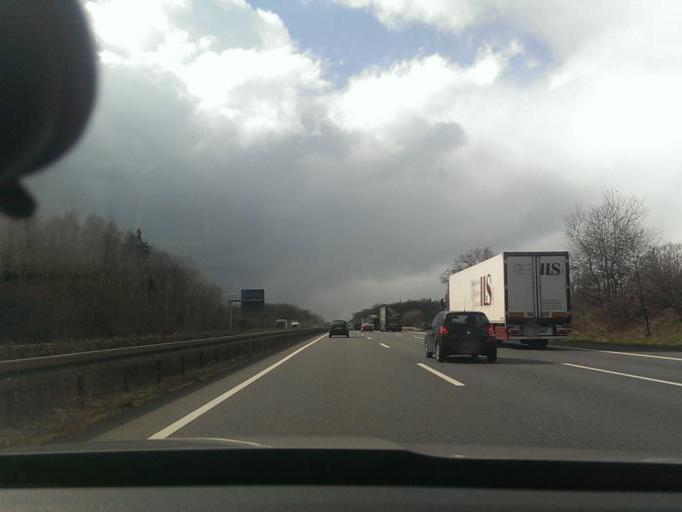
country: DE
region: Lower Saxony
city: Lehre
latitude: 52.3085
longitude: 10.6905
